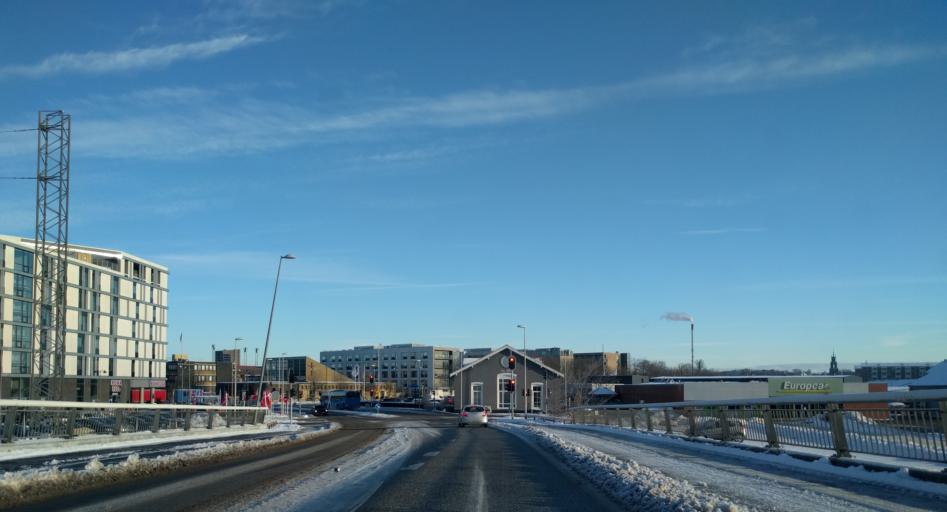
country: DK
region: North Denmark
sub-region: Alborg Kommune
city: Aalborg
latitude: 57.0413
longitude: 9.9239
